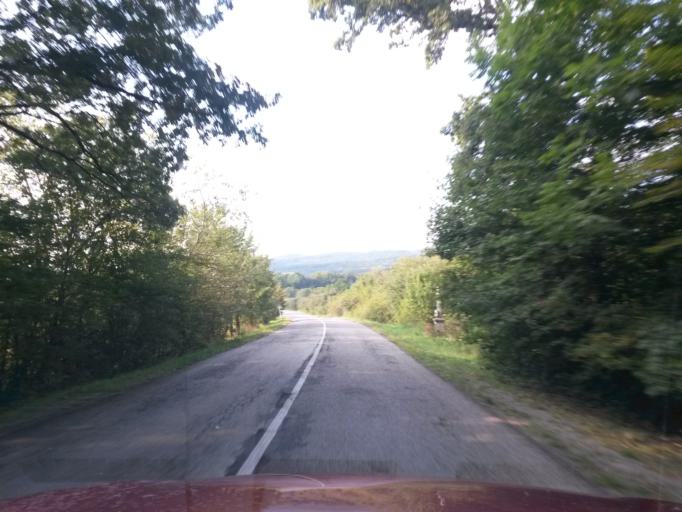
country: SK
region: Kosicky
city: Secovce
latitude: 48.7946
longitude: 21.4836
